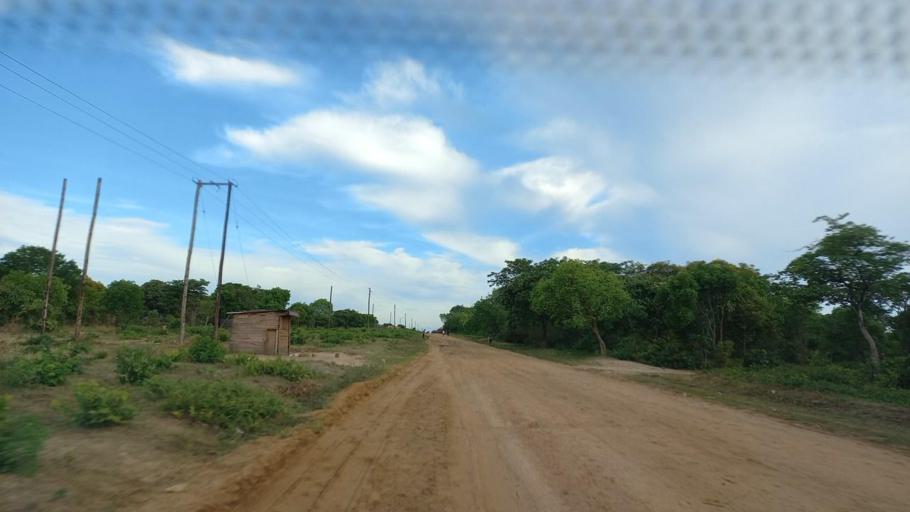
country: ZM
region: North-Western
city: Kabompo
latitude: -13.4223
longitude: 24.3234
